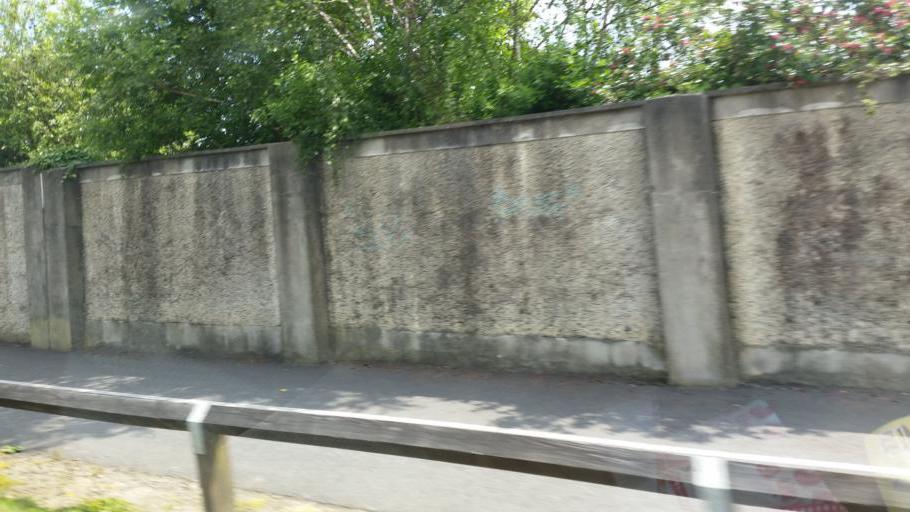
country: IE
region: Leinster
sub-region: Fingal County
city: Blanchardstown
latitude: 53.3880
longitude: -6.3901
